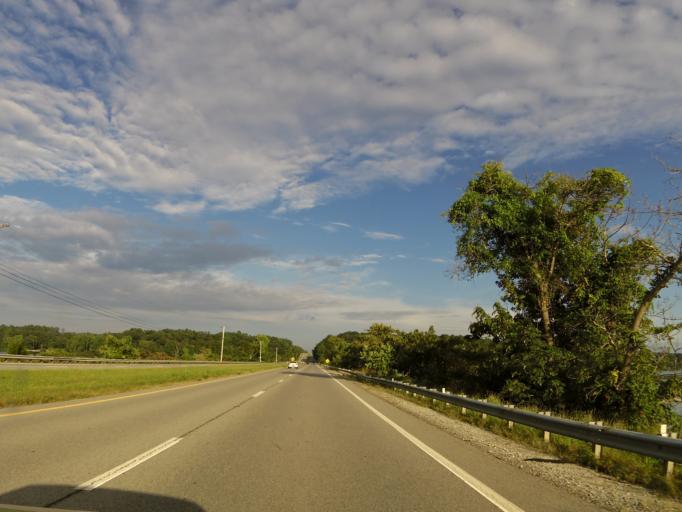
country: US
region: Alabama
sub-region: Lauderdale County
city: Rogersville
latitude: 34.8447
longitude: -87.3758
